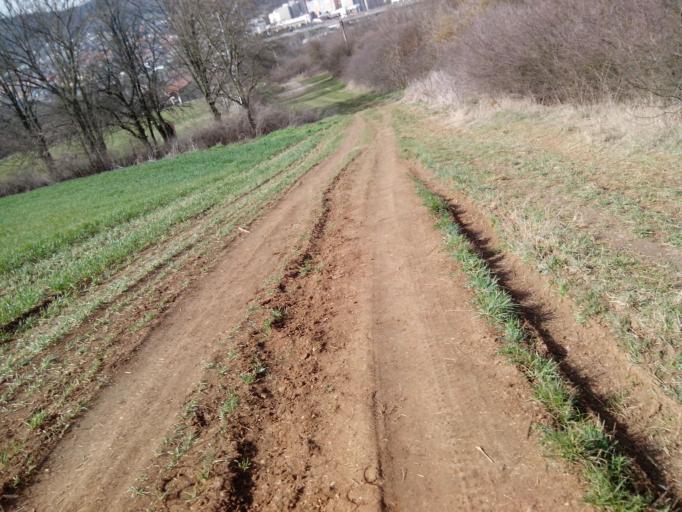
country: CZ
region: Central Bohemia
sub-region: Okres Beroun
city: Beroun
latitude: 49.9531
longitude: 14.0786
